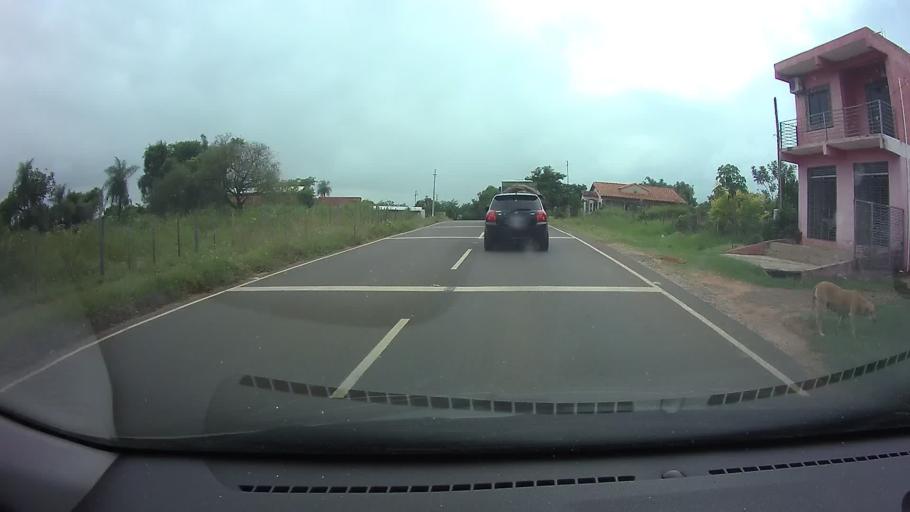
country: PY
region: Paraguari
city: Carapegua
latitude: -25.7596
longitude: -57.2534
